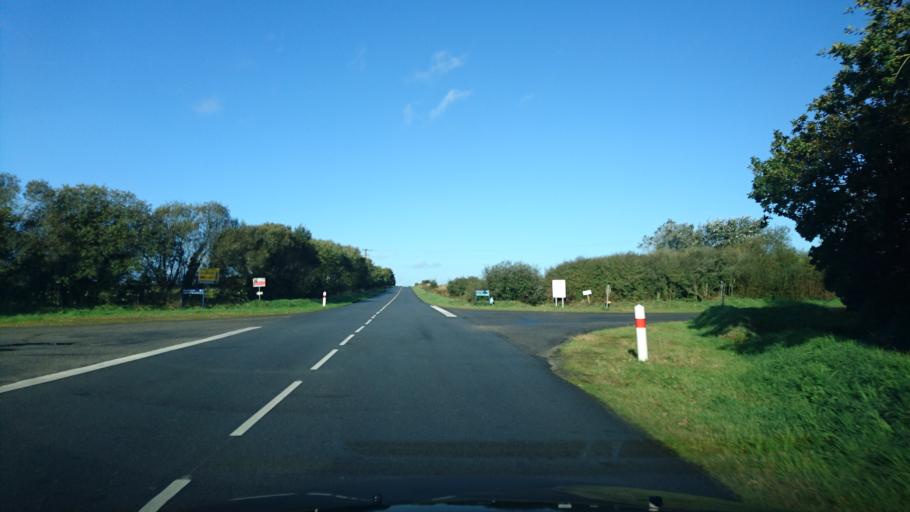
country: FR
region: Brittany
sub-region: Departement du Finistere
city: Plouarzel
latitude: 48.4384
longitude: -4.7315
